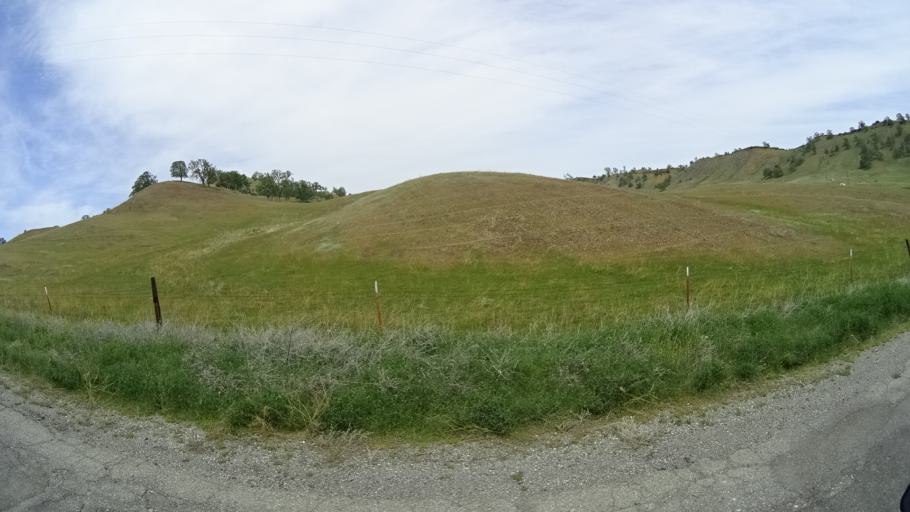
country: US
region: California
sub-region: Glenn County
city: Willows
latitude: 39.6162
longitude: -122.5900
